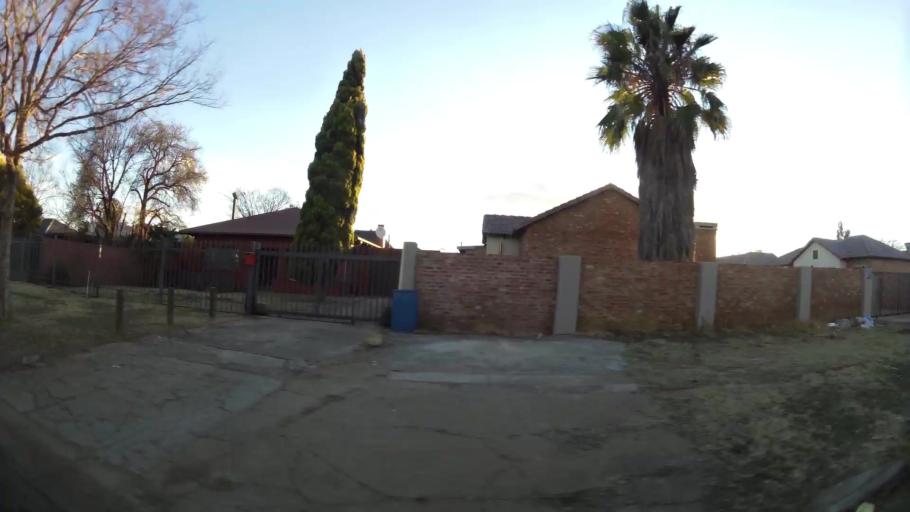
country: ZA
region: North-West
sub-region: Dr Kenneth Kaunda District Municipality
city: Potchefstroom
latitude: -26.7326
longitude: 27.0893
